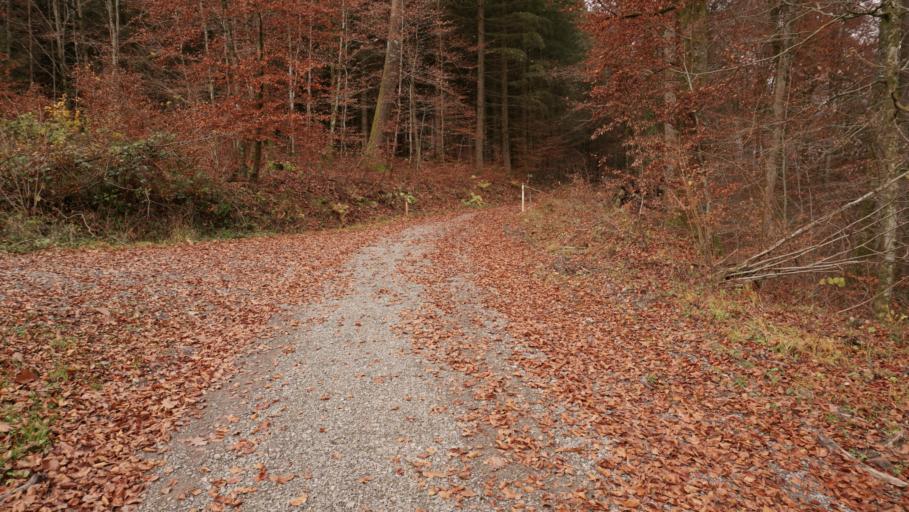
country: DE
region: Baden-Wuerttemberg
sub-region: Karlsruhe Region
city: Fahrenbach
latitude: 49.4243
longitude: 9.1163
